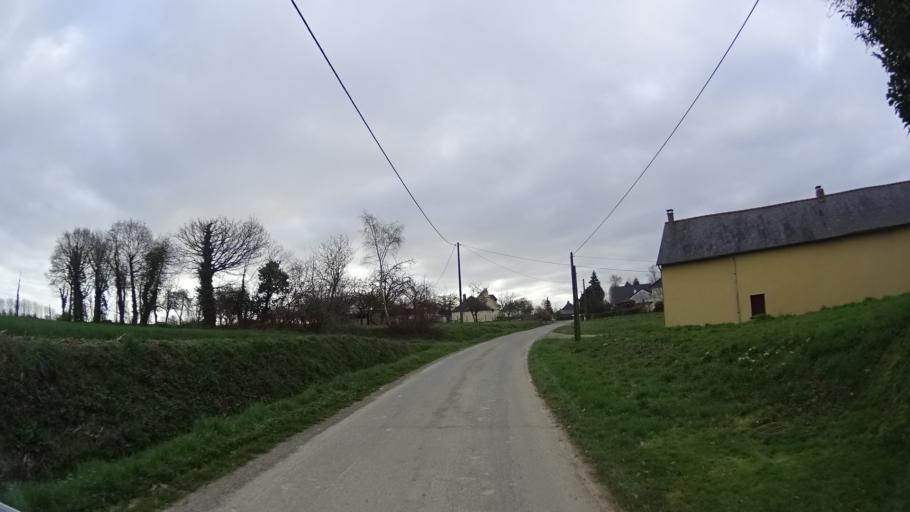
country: FR
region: Brittany
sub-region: Departement d'Ille-et-Vilaine
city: Romille
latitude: 48.1820
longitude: -1.8628
